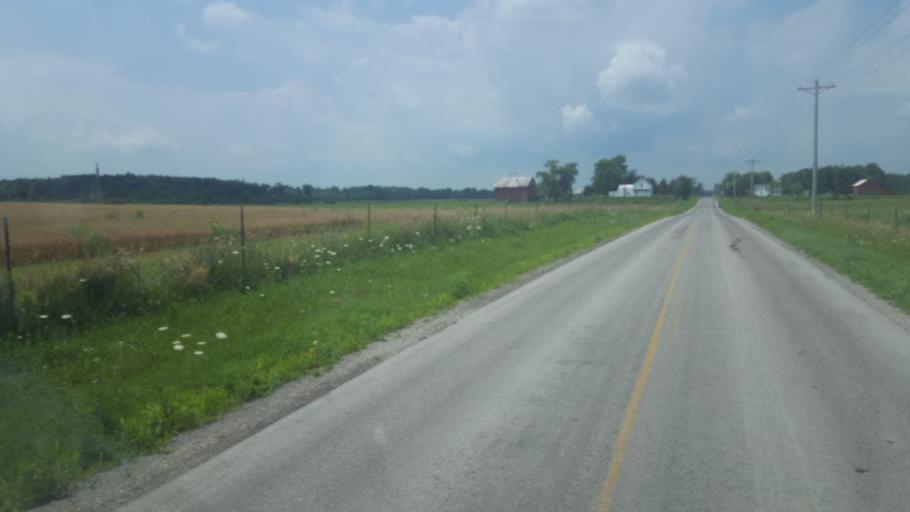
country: US
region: Ohio
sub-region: Hardin County
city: Kenton
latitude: 40.5901
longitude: -83.4552
